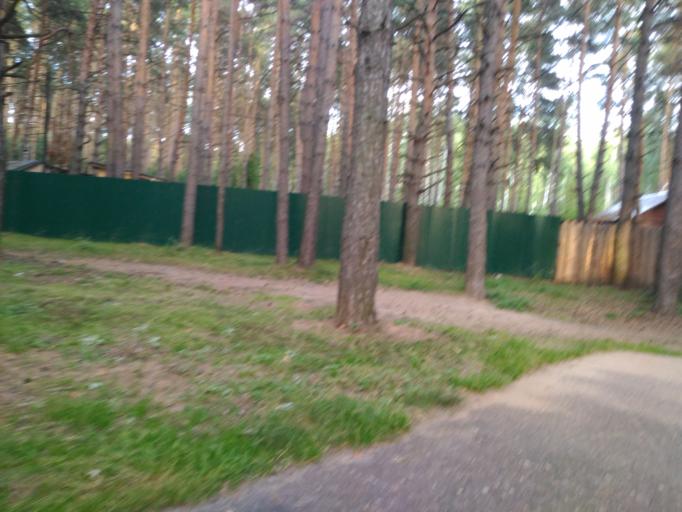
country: RU
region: Ulyanovsk
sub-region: Ulyanovskiy Rayon
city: Ulyanovsk
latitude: 54.3599
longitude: 48.5153
